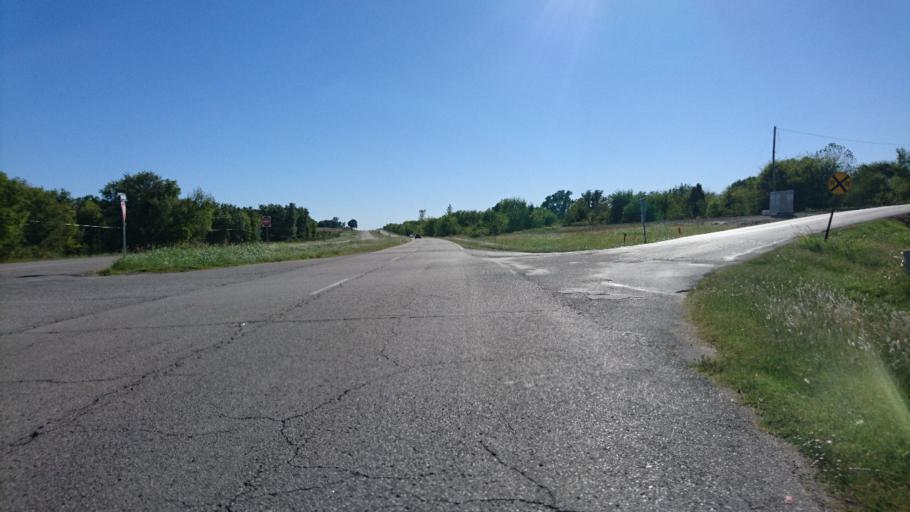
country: US
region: Oklahoma
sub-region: Rogers County
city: Bushyhead
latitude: 36.4235
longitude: -95.5320
